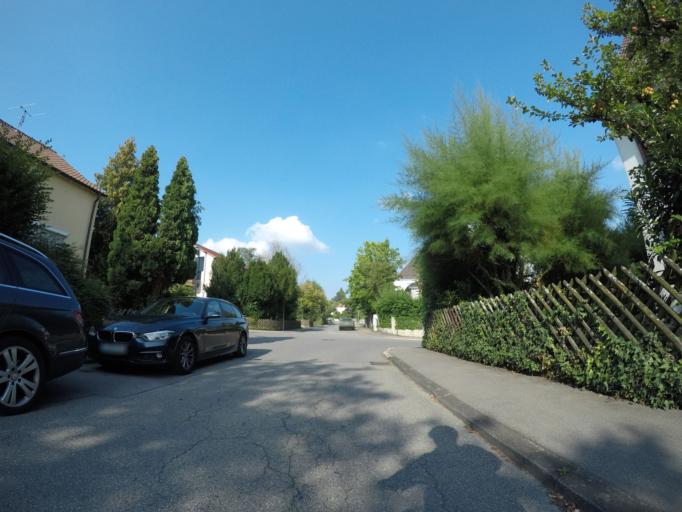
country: DE
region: Baden-Wuerttemberg
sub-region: Tuebingen Region
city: Reutlingen
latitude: 48.4839
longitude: 9.2008
